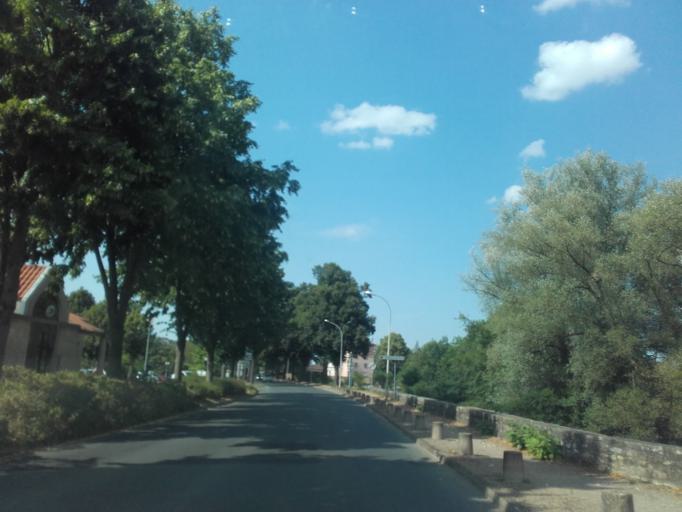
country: FR
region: Bourgogne
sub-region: Departement de Saone-et-Loire
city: Cluny
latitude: 46.4323
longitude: 4.6640
